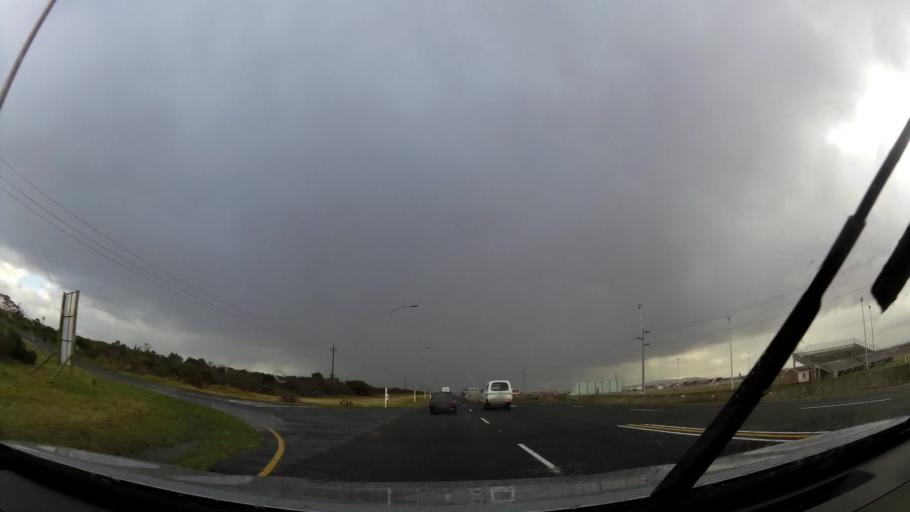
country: ZA
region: Western Cape
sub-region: Eden District Municipality
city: Mossel Bay
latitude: -34.1828
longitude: 22.0971
